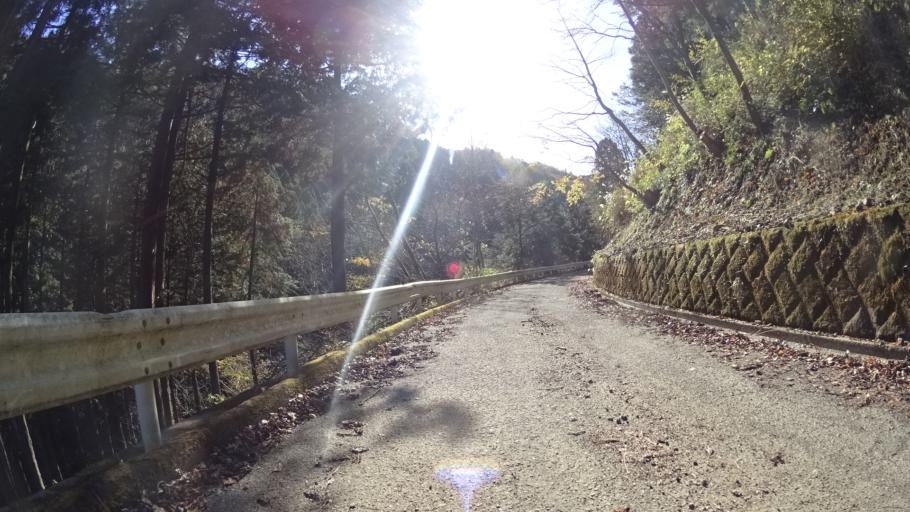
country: JP
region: Kanagawa
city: Atsugi
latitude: 35.5176
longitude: 139.2740
